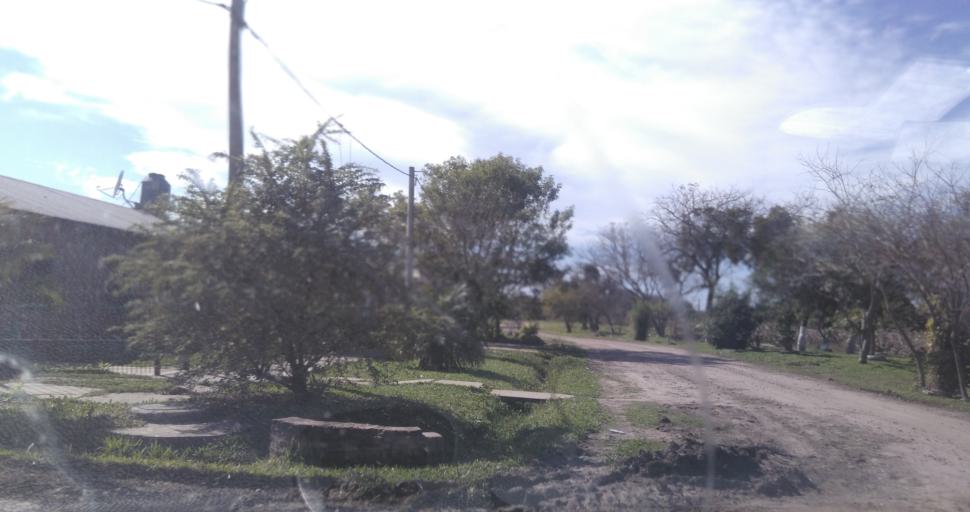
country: AR
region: Chaco
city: Fontana
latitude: -27.4389
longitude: -59.0265
